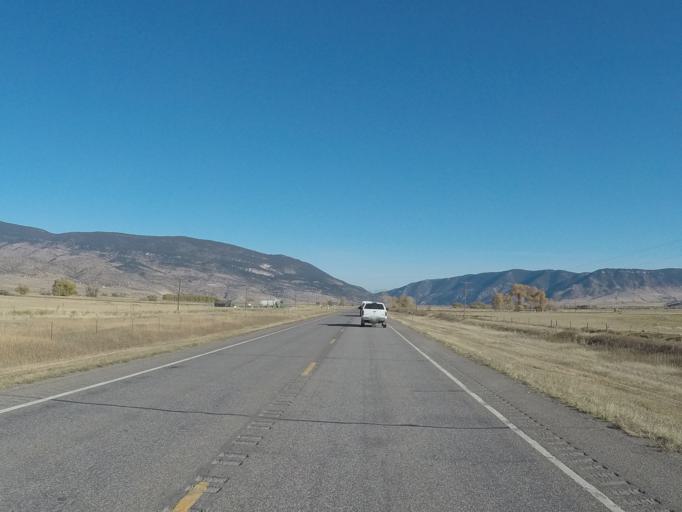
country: US
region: Montana
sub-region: Park County
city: Livingston
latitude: 45.5226
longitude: -110.6085
